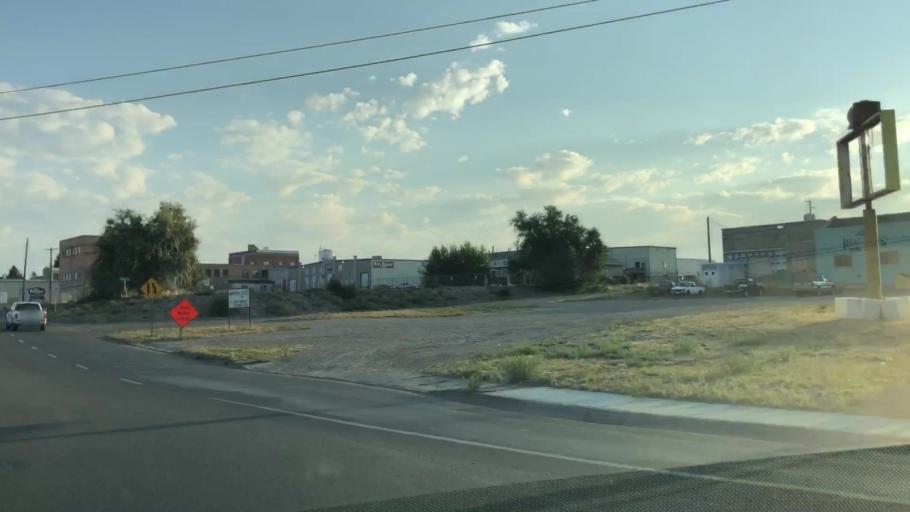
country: US
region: Idaho
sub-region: Bonneville County
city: Idaho Falls
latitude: 43.4845
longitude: -112.0471
